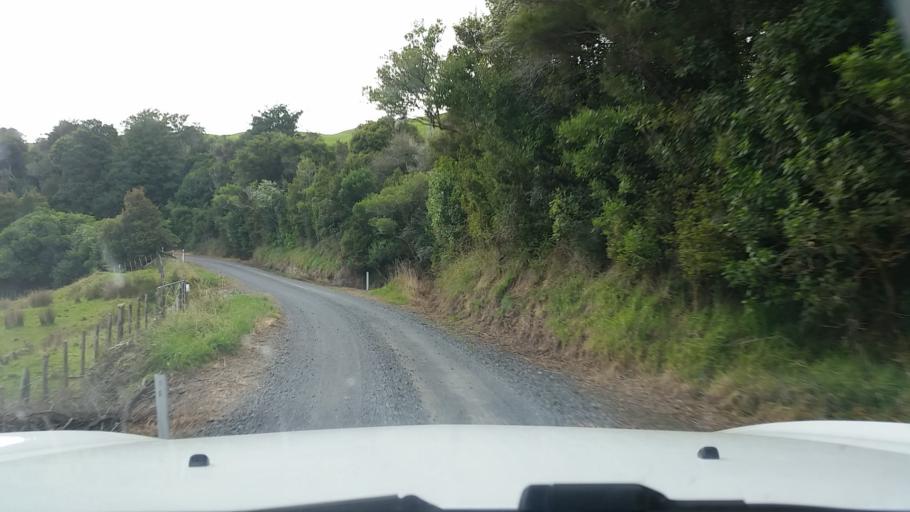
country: NZ
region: Waikato
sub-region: Hauraki District
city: Ngatea
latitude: -37.4794
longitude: 175.4539
